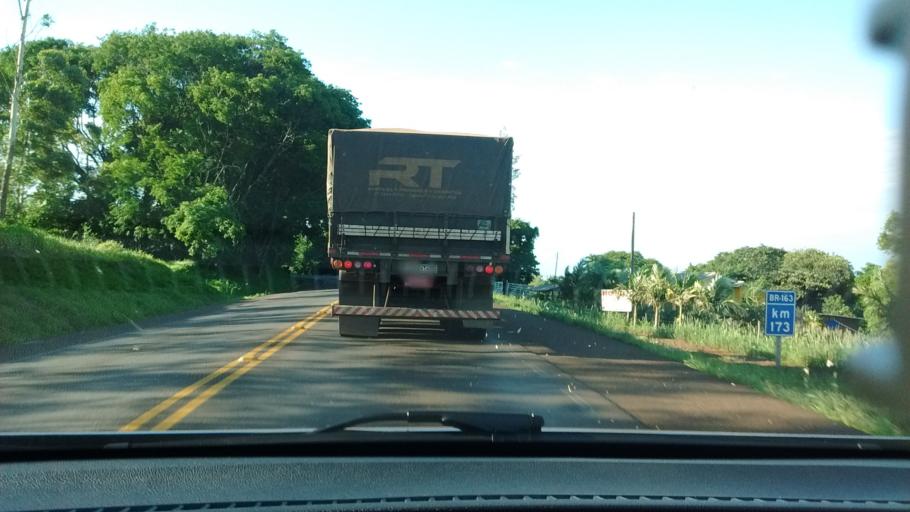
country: BR
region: Parana
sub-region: Cascavel
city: Cascavel
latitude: -25.2357
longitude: -53.5900
